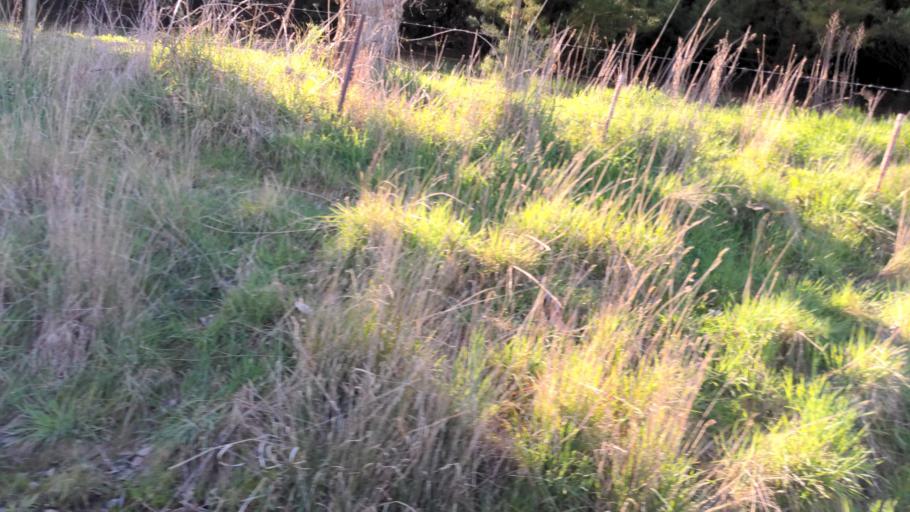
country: AU
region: New South Wales
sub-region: Blayney
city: Blayney
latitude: -33.4134
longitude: 149.3212
